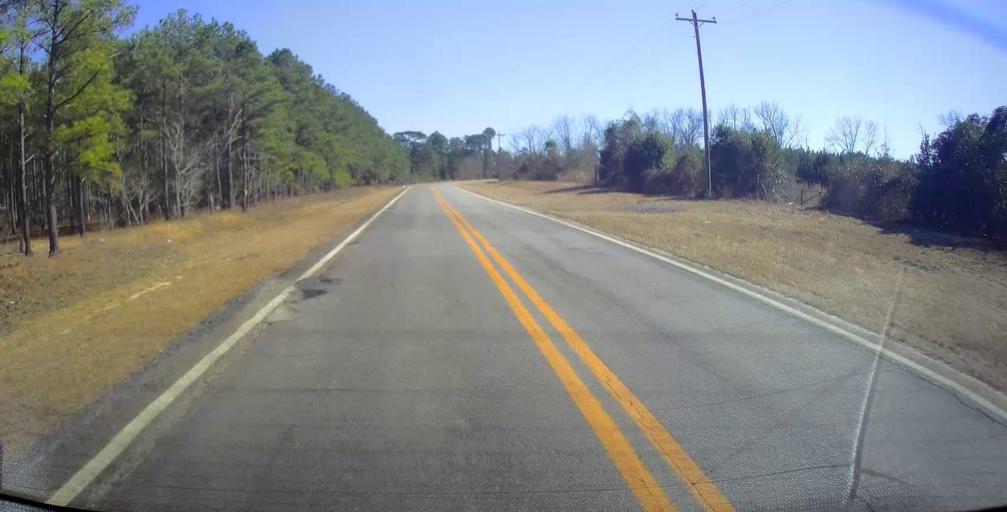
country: US
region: Georgia
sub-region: Crawford County
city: Roberta
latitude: 32.6315
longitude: -83.9921
